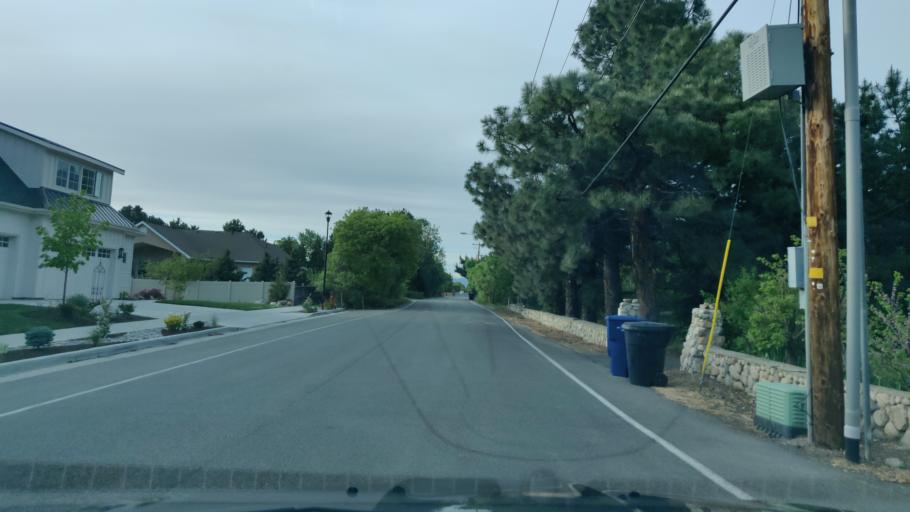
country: US
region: Utah
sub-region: Salt Lake County
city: Granite
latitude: 40.5755
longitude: -111.8056
